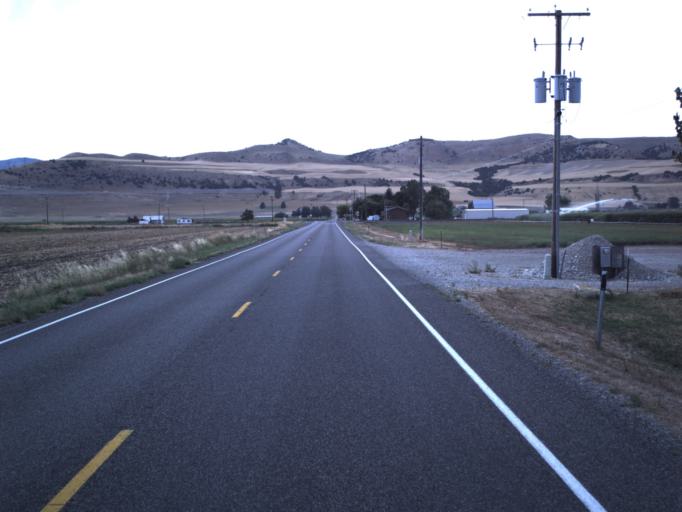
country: US
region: Utah
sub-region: Cache County
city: Lewiston
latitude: 41.9754
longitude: -111.9480
